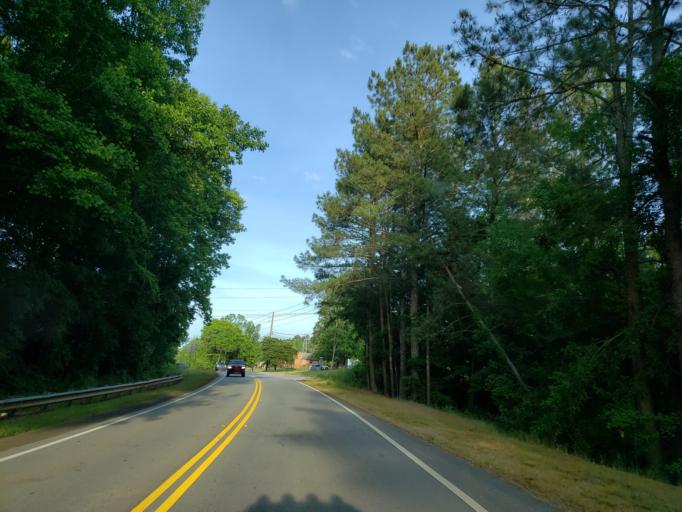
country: US
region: Georgia
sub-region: Carroll County
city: Carrollton
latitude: 33.5922
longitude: -85.1289
